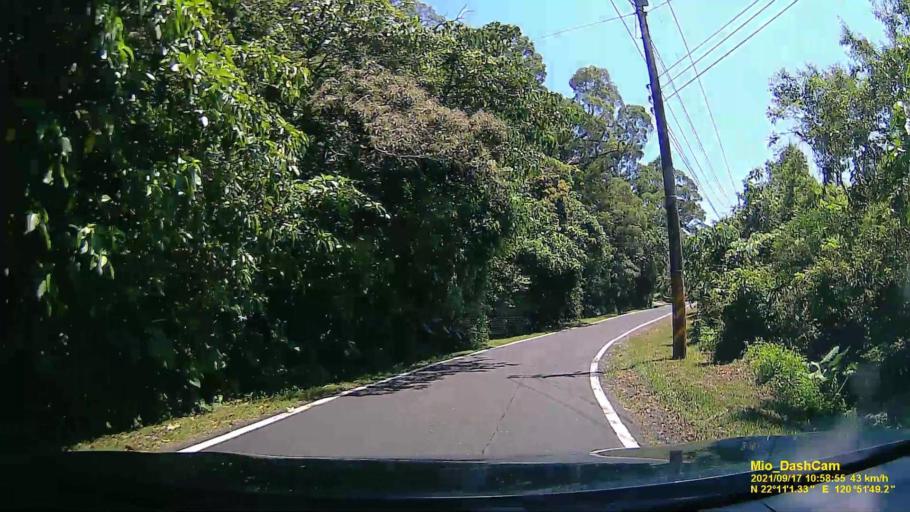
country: TW
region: Taiwan
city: Hengchun
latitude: 22.1837
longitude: 120.8637
